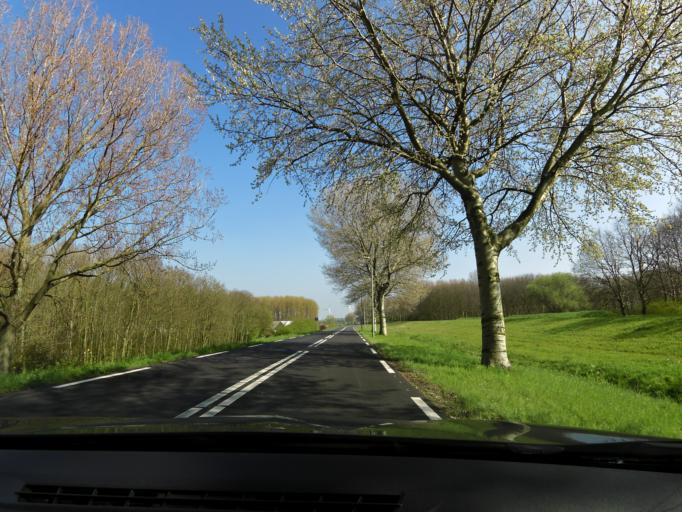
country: NL
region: South Holland
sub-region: Gemeente Maassluis
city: Maassluis
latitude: 51.9082
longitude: 4.2770
